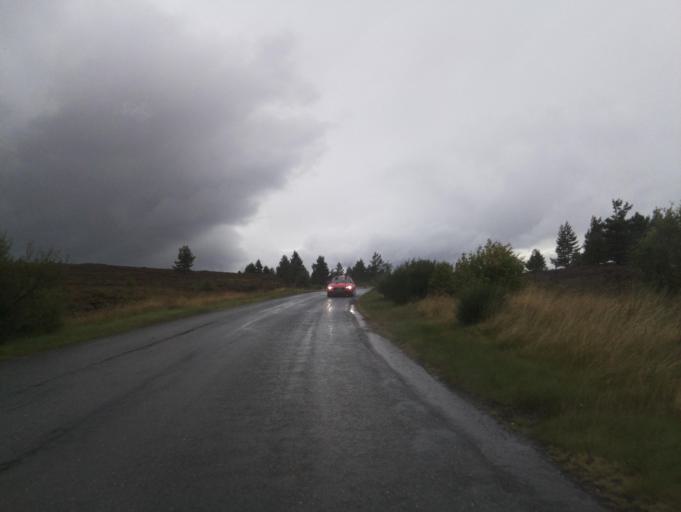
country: GB
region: Scotland
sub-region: Highland
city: Grantown on Spey
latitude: 57.2818
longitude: -3.5560
